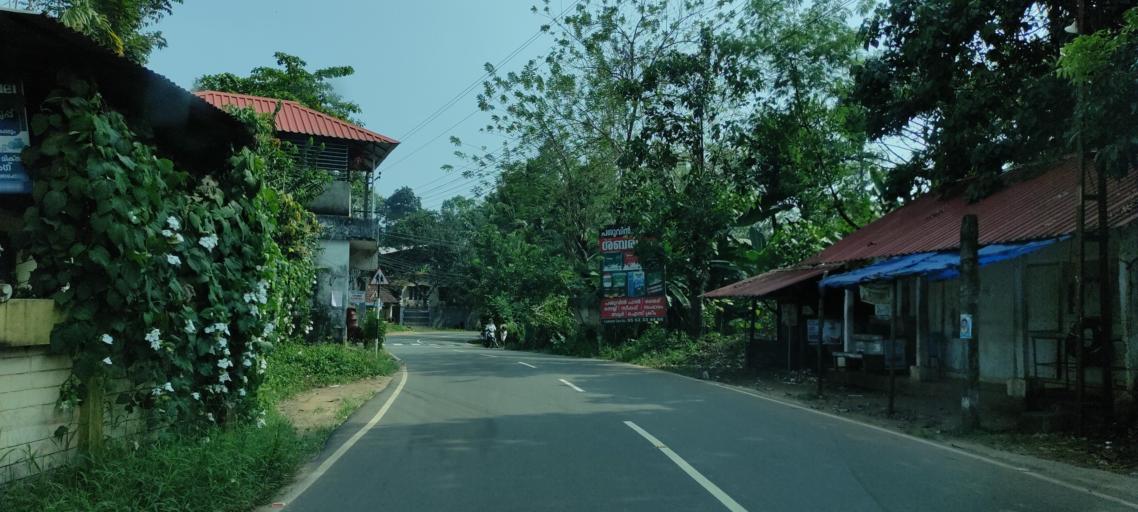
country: IN
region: Kerala
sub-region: Pattanamtitta
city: Adur
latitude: 9.2430
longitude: 76.6809
